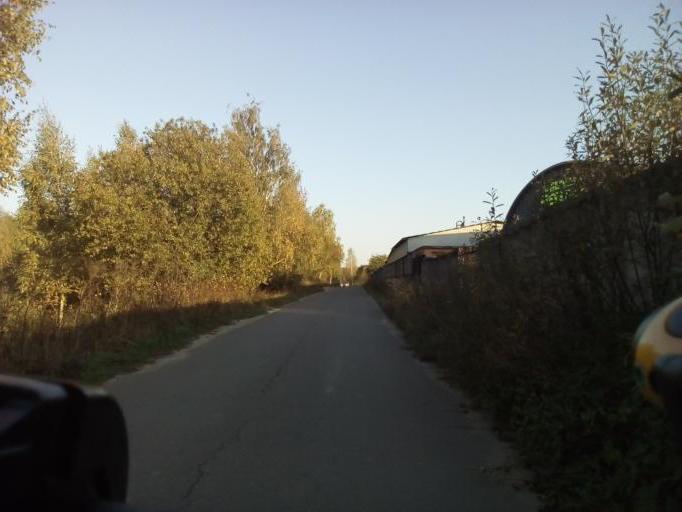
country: RU
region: Moskovskaya
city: Ramenskoye
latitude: 55.6053
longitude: 38.2810
